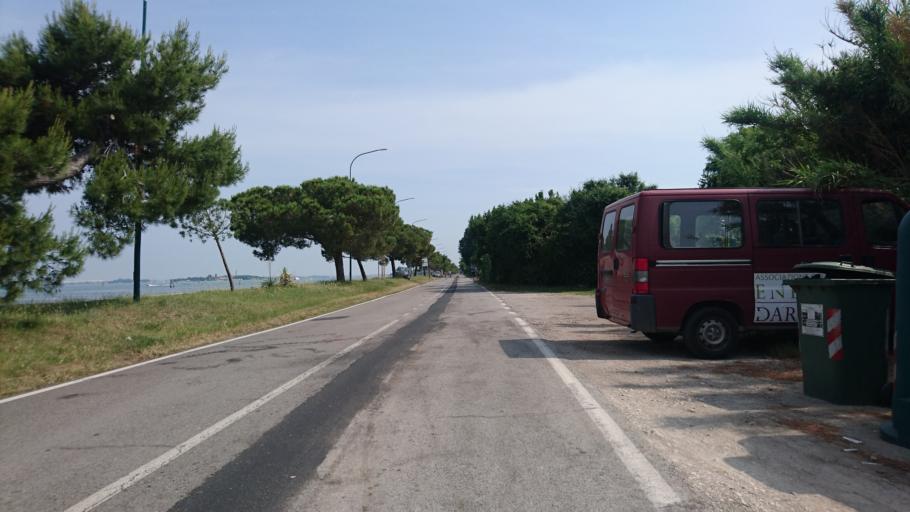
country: IT
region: Veneto
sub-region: Provincia di Venezia
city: San Pietro in Volta
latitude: 45.3601
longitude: 12.3317
